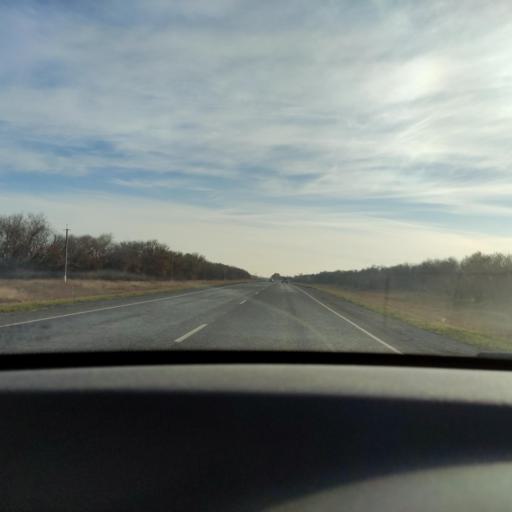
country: RU
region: Samara
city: Krasnoarmeyskoye
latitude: 52.7900
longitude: 50.0175
